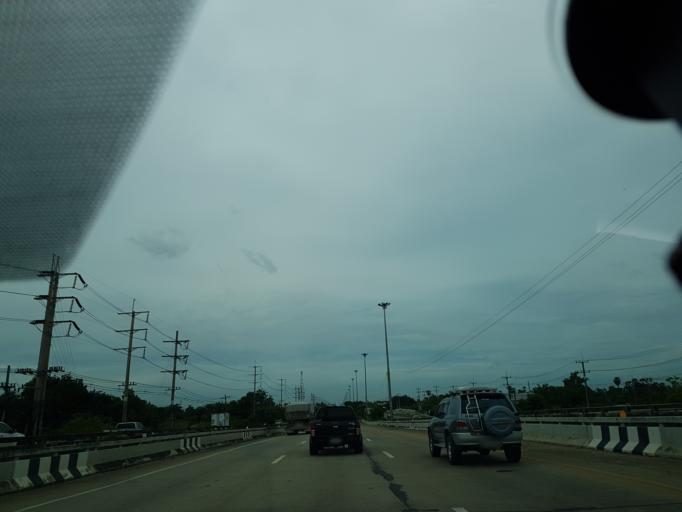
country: TH
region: Pathum Thani
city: Pathum Thani
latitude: 14.0383
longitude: 100.5619
